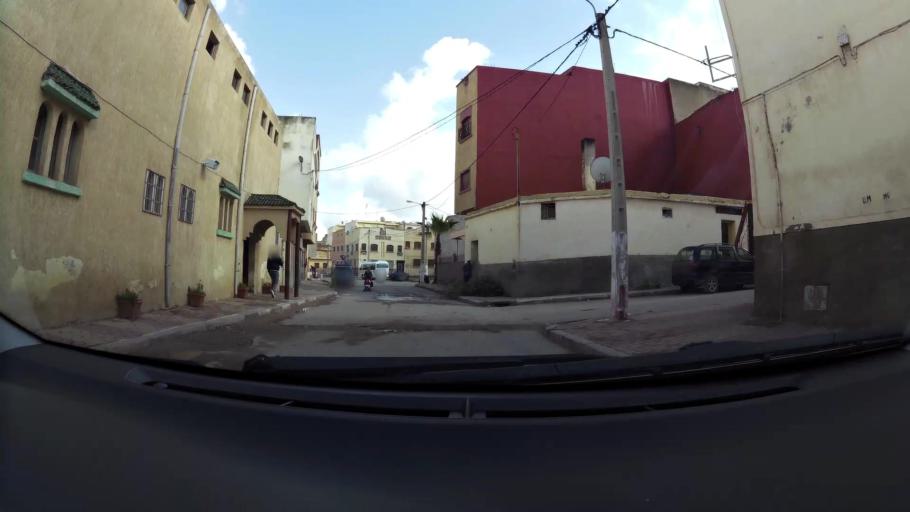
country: MA
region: Chaouia-Ouardigha
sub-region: Settat Province
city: Settat
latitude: 33.0108
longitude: -7.6260
